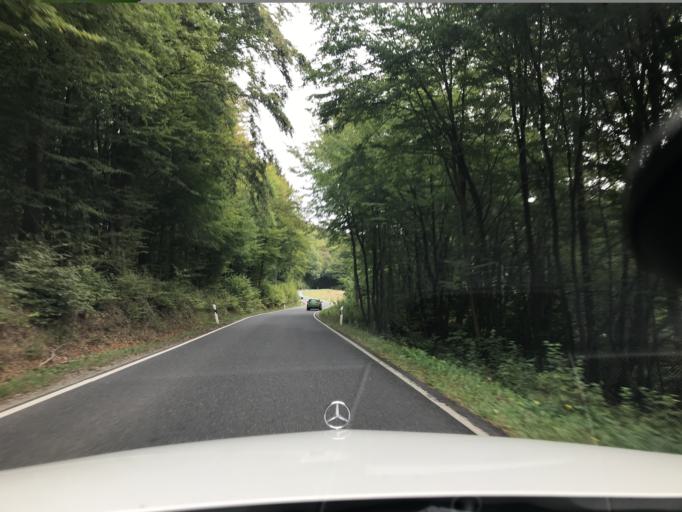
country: DE
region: Hesse
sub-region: Regierungsbezirk Kassel
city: Helsa
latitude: 51.2458
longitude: 9.7036
